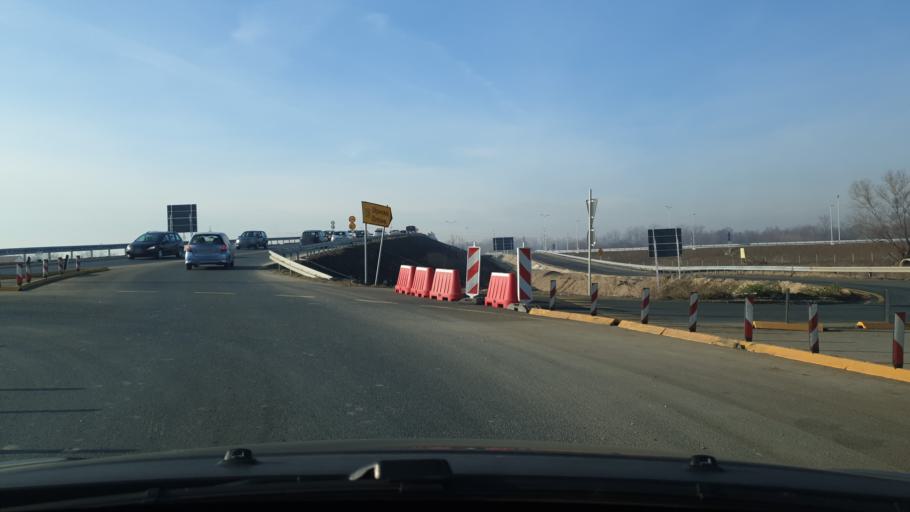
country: RS
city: Baric
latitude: 44.6499
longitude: 20.2323
